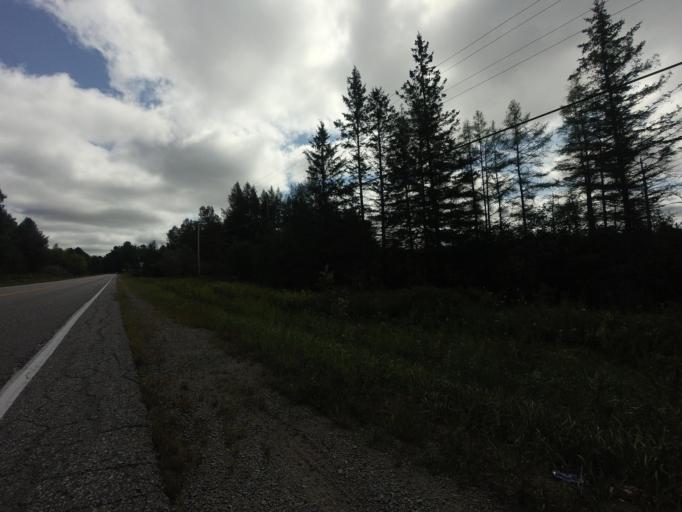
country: CA
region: Ontario
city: Omemee
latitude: 44.8025
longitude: -78.6237
